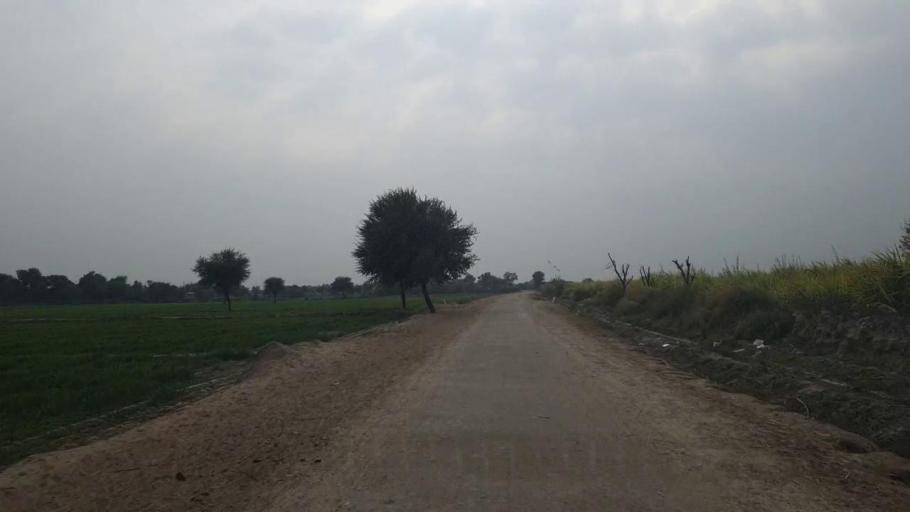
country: PK
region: Sindh
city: Shahdadpur
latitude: 25.9486
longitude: 68.7028
